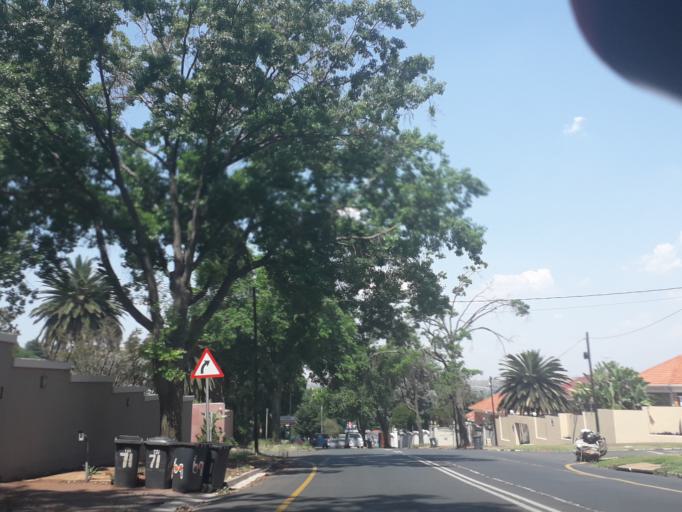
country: ZA
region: Gauteng
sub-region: City of Johannesburg Metropolitan Municipality
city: Johannesburg
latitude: -26.1711
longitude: 28.0946
